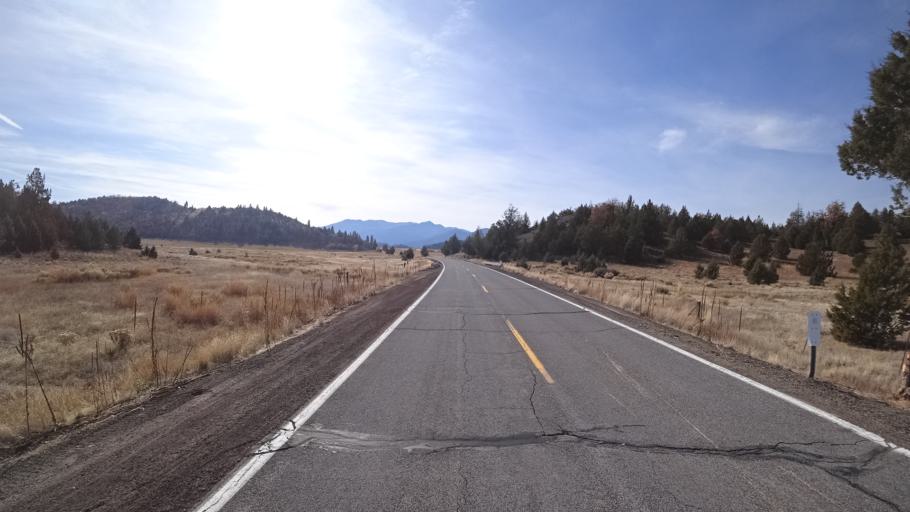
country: US
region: California
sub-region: Siskiyou County
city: Weed
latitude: 41.4871
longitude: -122.4079
